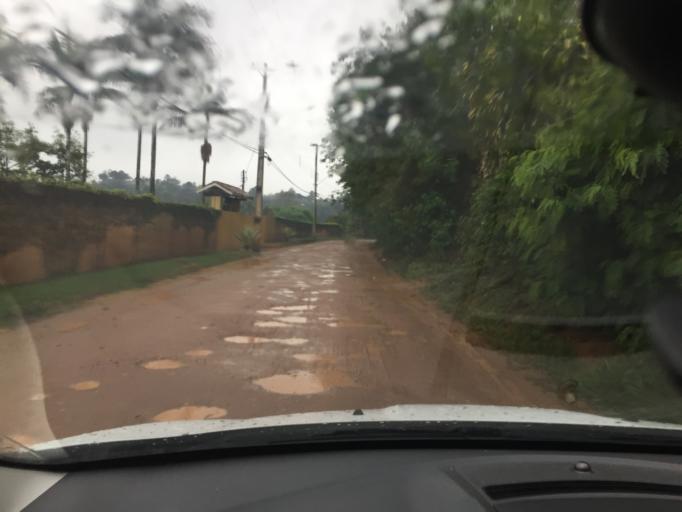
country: BR
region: Sao Paulo
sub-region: Jarinu
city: Jarinu
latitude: -23.1374
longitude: -46.7229
